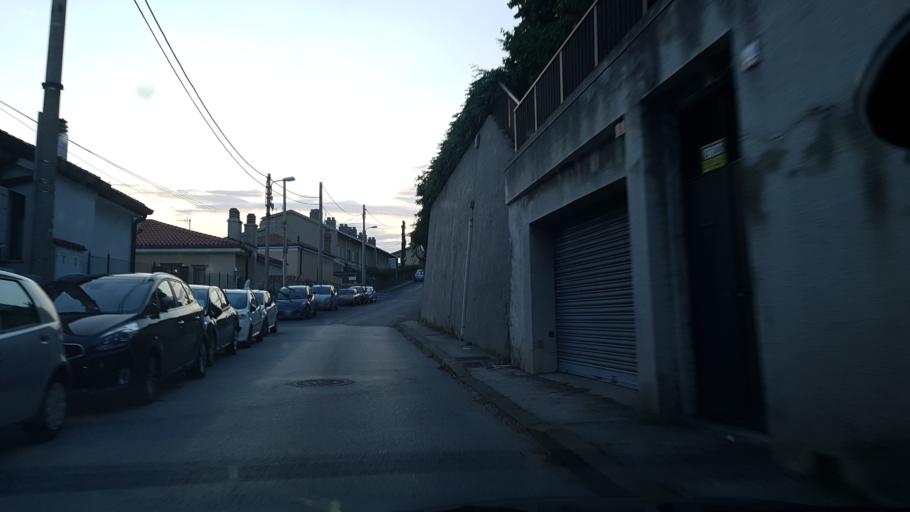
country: IT
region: Friuli Venezia Giulia
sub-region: Provincia di Trieste
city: Villa Opicina
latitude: 45.6720
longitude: 13.7632
